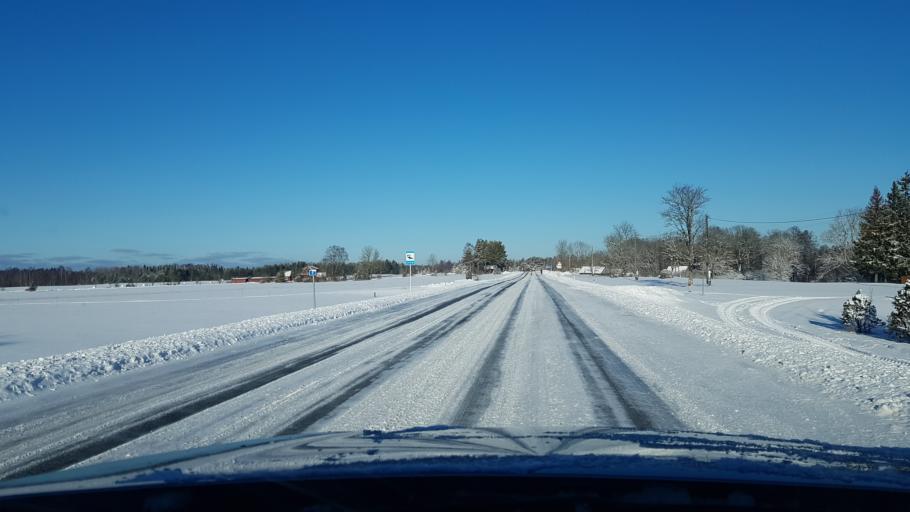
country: EE
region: Hiiumaa
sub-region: Kaerdla linn
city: Kardla
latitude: 58.9528
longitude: 22.7726
